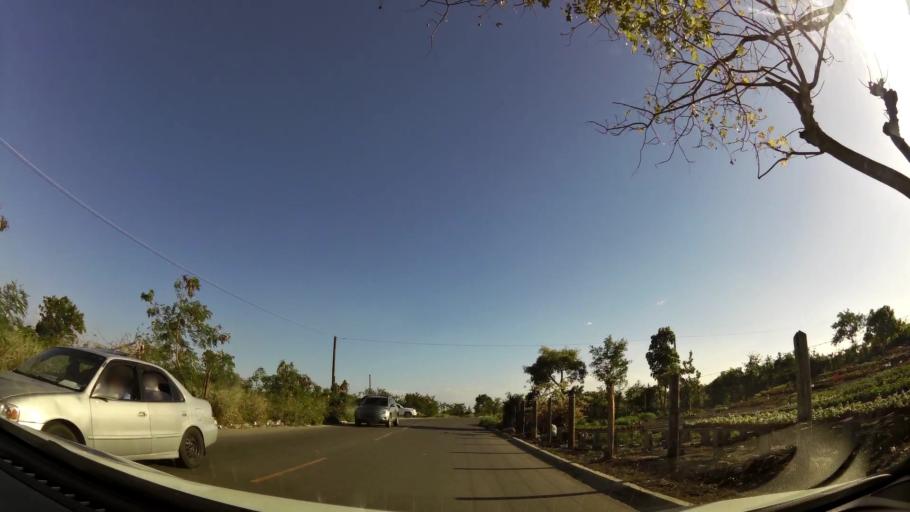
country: DO
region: Santo Domingo
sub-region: Santo Domingo
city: Santo Domingo Este
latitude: 18.4835
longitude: -69.8057
